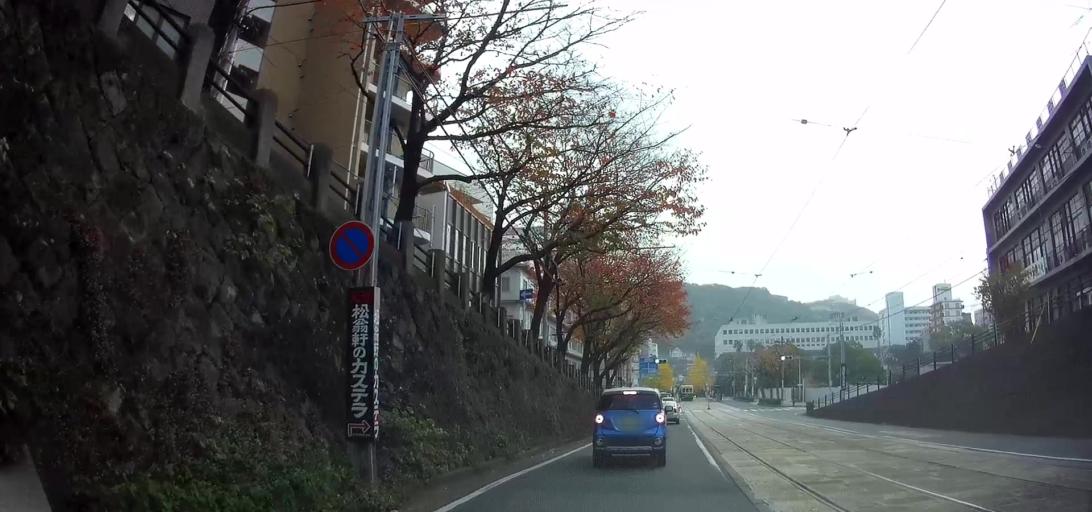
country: JP
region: Nagasaki
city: Nagasaki-shi
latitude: 32.7502
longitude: 129.8797
